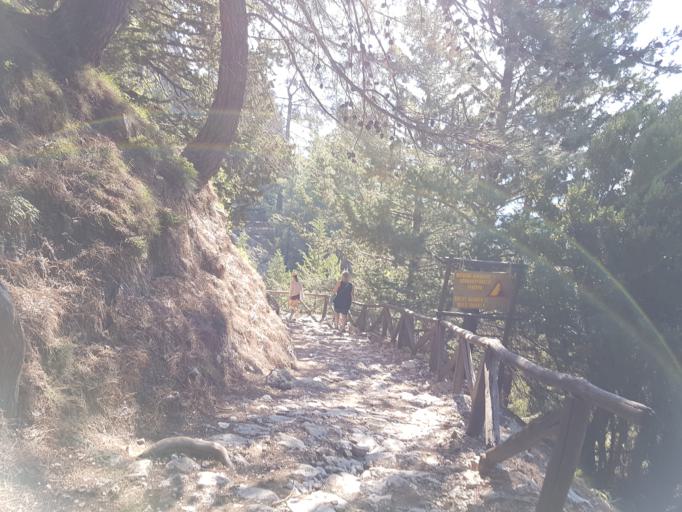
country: GR
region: Crete
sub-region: Nomos Chanias
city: Perivolia
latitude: 35.3088
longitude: 23.9231
